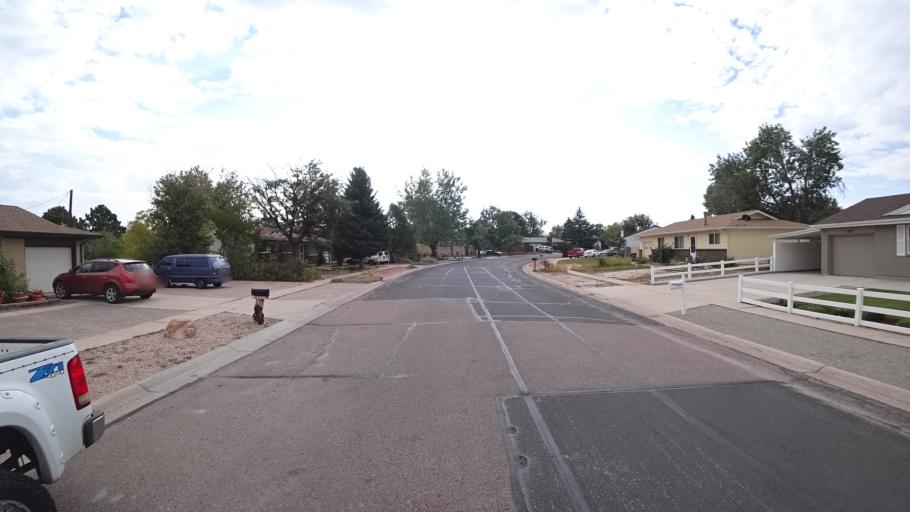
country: US
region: Colorado
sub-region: El Paso County
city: Cimarron Hills
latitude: 38.8455
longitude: -104.7505
